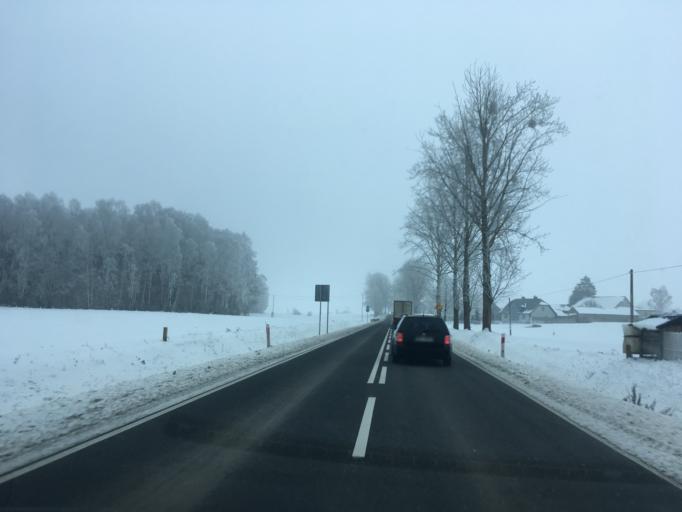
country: PL
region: Warmian-Masurian Voivodeship
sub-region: Powiat dzialdowski
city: Lidzbark
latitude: 53.2468
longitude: 19.9177
